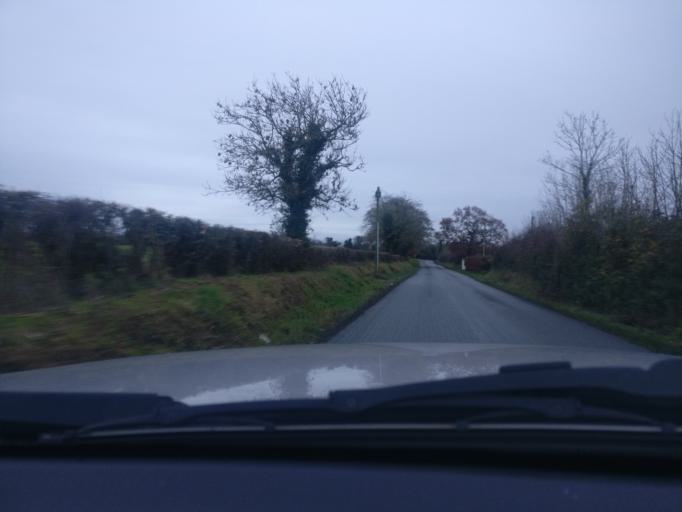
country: IE
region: Leinster
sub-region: Kildare
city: Maynooth
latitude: 53.4186
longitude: -6.6129
